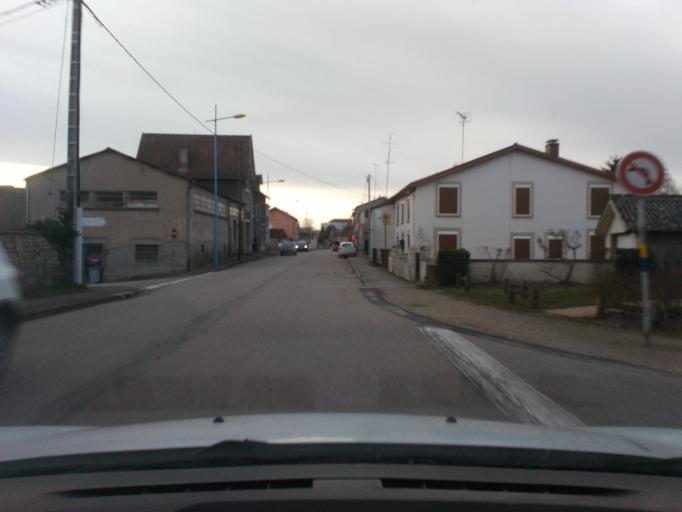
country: FR
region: Lorraine
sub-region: Departement des Vosges
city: Charmes
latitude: 48.3754
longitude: 6.3010
